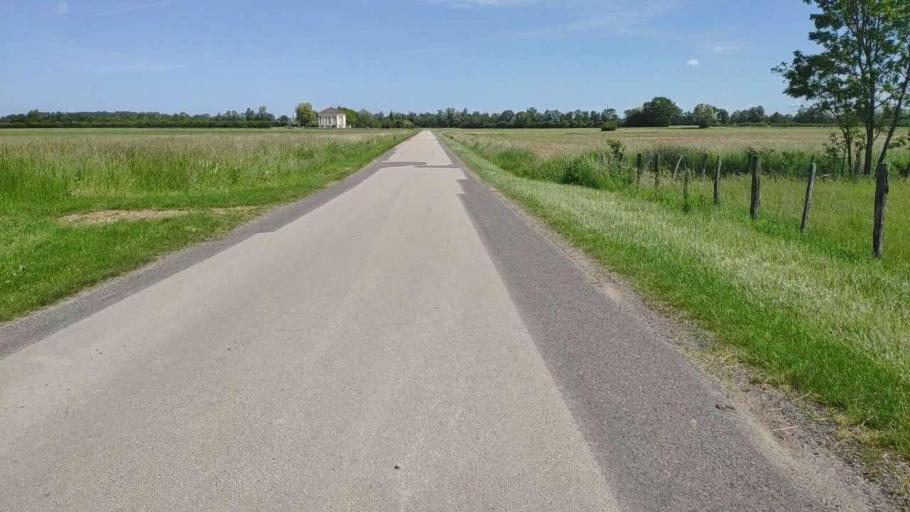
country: FR
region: Franche-Comte
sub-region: Departement du Jura
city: Bletterans
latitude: 46.7180
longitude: 5.4433
